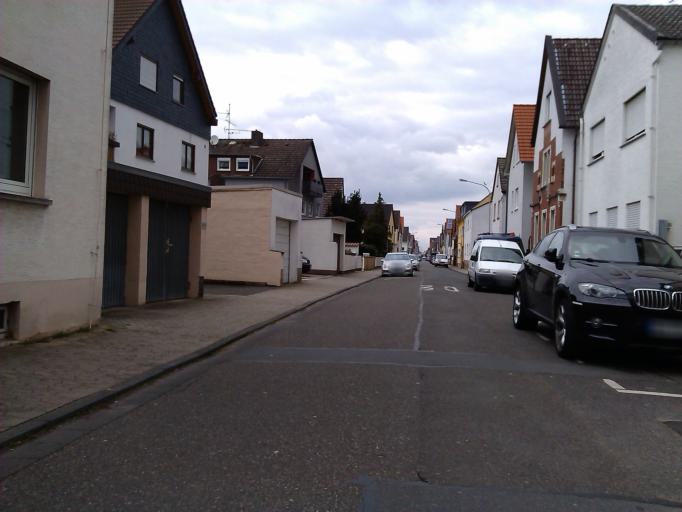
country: DE
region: Hesse
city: Griesheim
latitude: 49.8556
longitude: 8.5595
